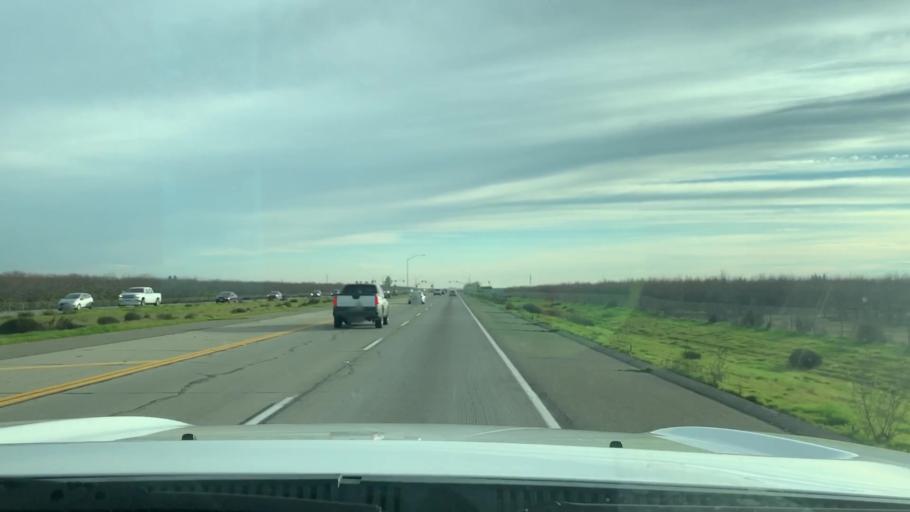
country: US
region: California
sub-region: Fresno County
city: Caruthers
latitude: 36.5225
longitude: -119.7864
